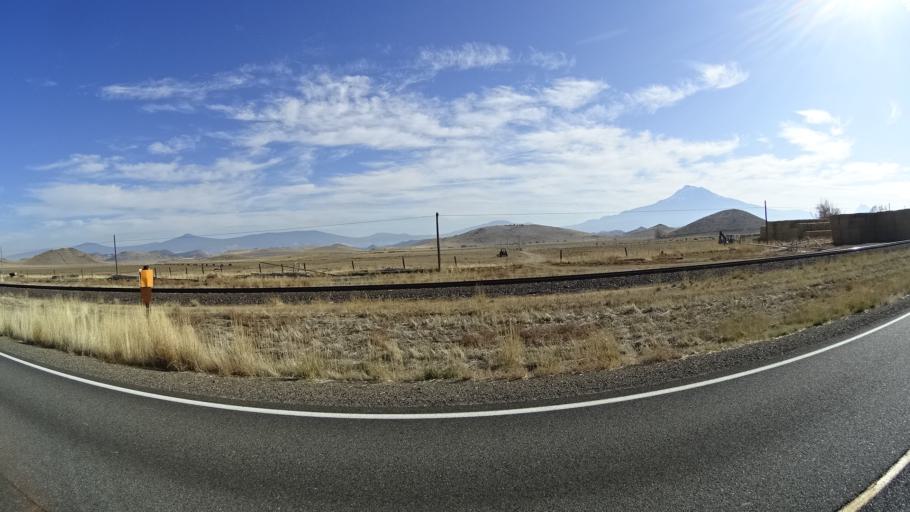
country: US
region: California
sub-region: Siskiyou County
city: Montague
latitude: 41.5456
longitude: -122.5260
